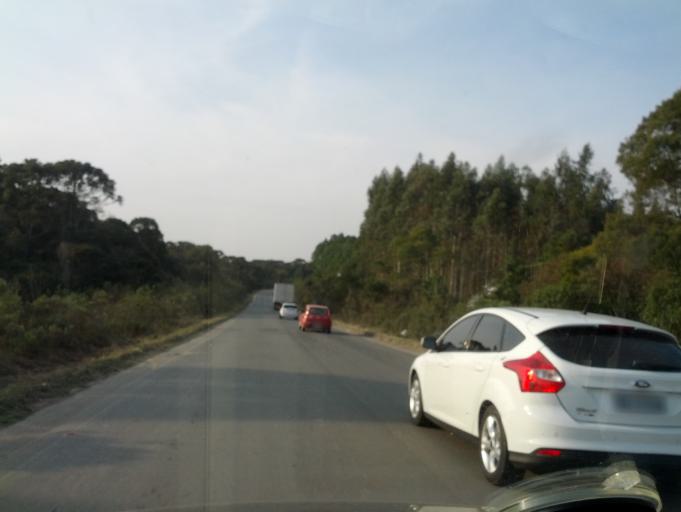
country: BR
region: Santa Catarina
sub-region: Otacilio Costa
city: Otacilio Costa
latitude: -27.5356
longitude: -50.1431
